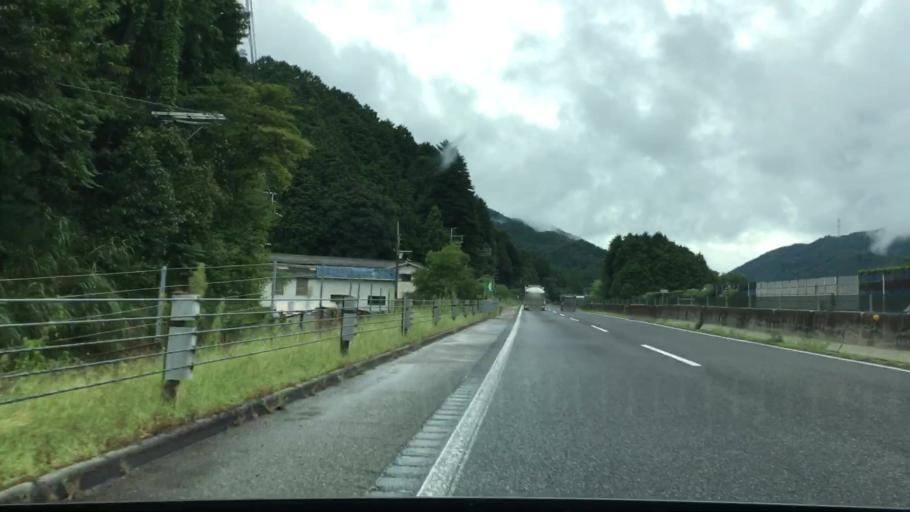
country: JP
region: Hyogo
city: Yamazakicho-nakabirose
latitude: 35.0208
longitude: 134.4997
